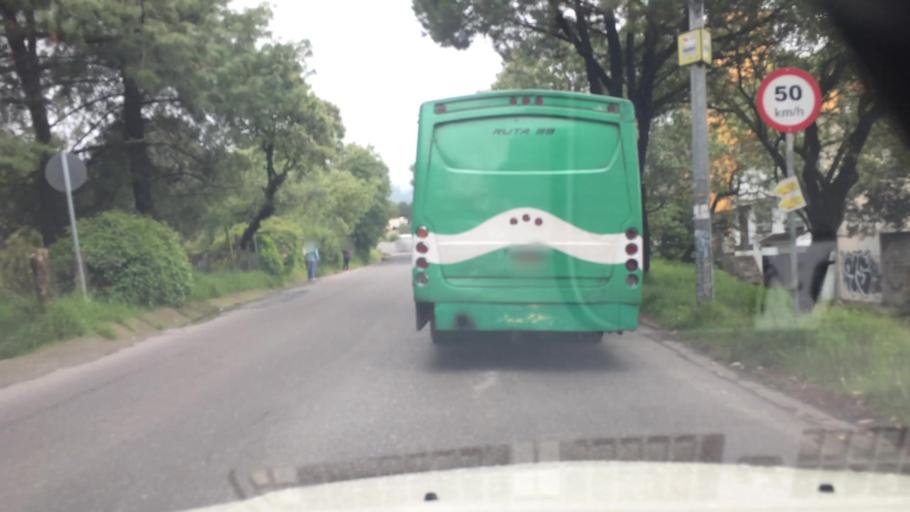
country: MX
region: Mexico City
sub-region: Tlalpan
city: Lomas de Tepemecatl
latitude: 19.2656
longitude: -99.2385
